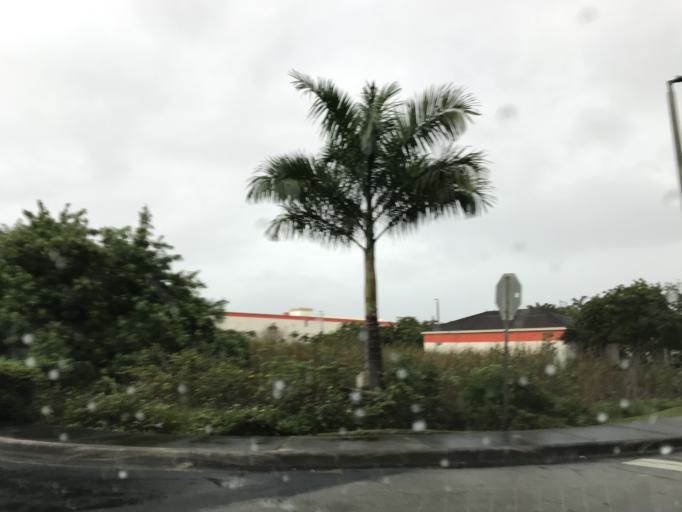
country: US
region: Florida
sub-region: Broward County
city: Coral Springs
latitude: 26.3064
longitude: -80.2808
